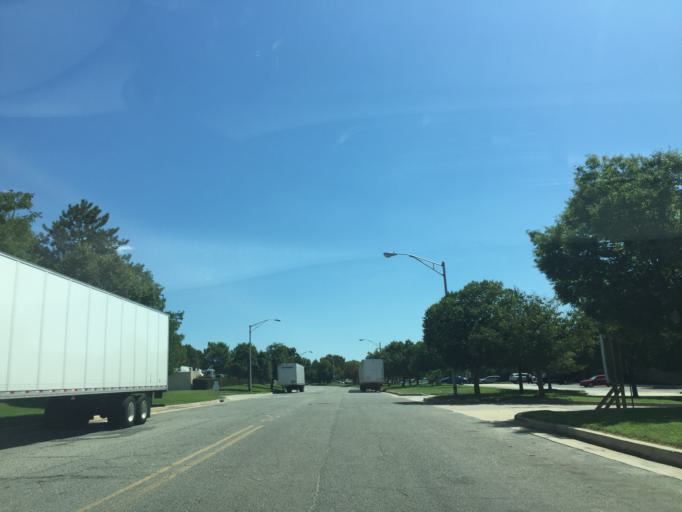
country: US
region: Maryland
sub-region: Baltimore County
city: Dundalk
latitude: 39.2708
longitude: -76.5385
